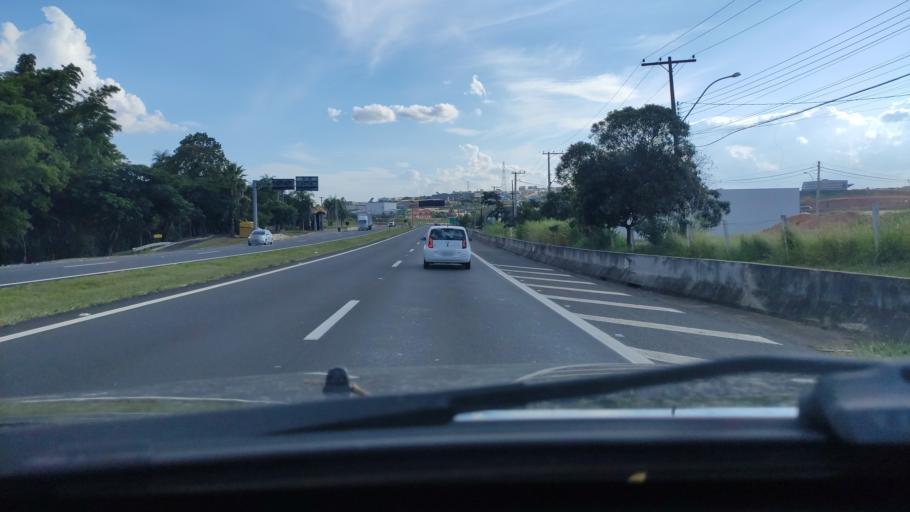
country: BR
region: Sao Paulo
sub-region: Itapira
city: Itapira
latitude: -22.4485
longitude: -46.8360
